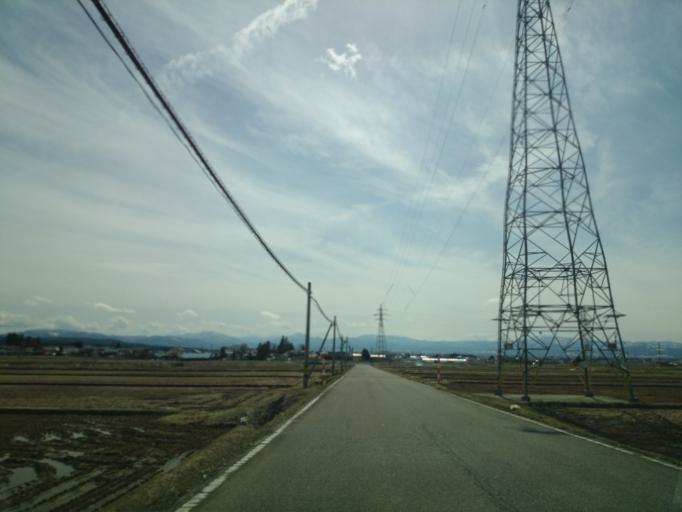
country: JP
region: Fukushima
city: Kitakata
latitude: 37.6486
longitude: 139.9107
